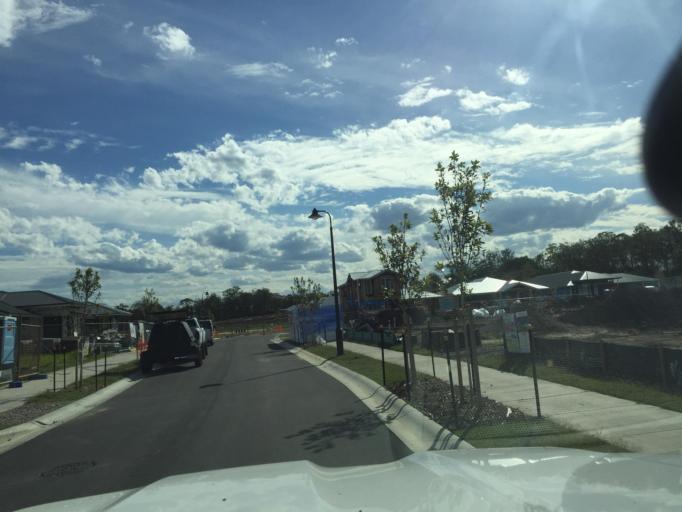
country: AU
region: Queensland
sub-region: Moreton Bay
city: Morayfield
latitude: -27.1249
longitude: 152.9958
